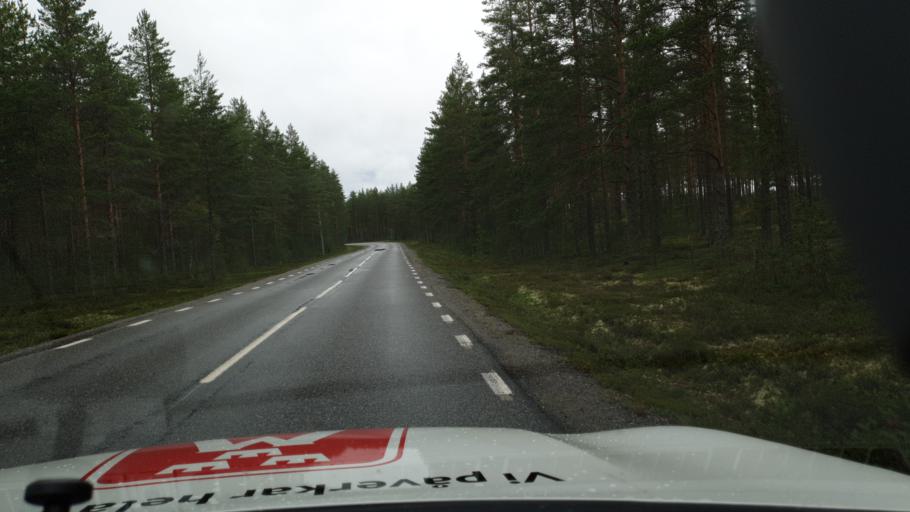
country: SE
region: Vaesterbotten
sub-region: Umea Kommun
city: Saevar
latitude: 63.9949
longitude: 20.4950
